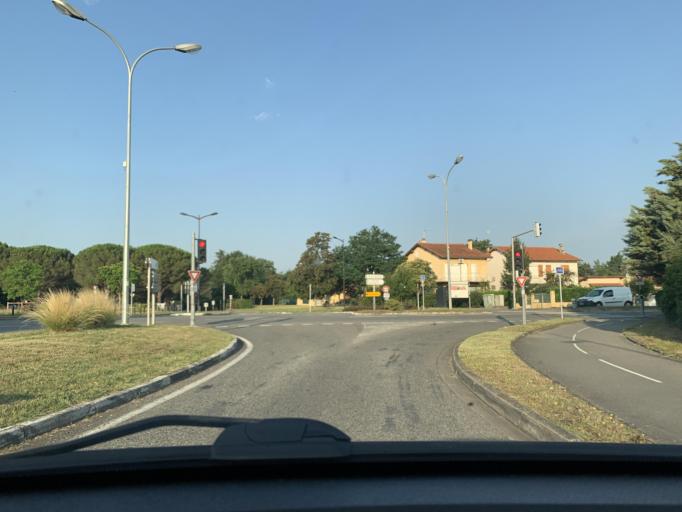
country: FR
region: Midi-Pyrenees
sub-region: Departement de la Haute-Garonne
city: Labege
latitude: 43.5322
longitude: 1.5344
